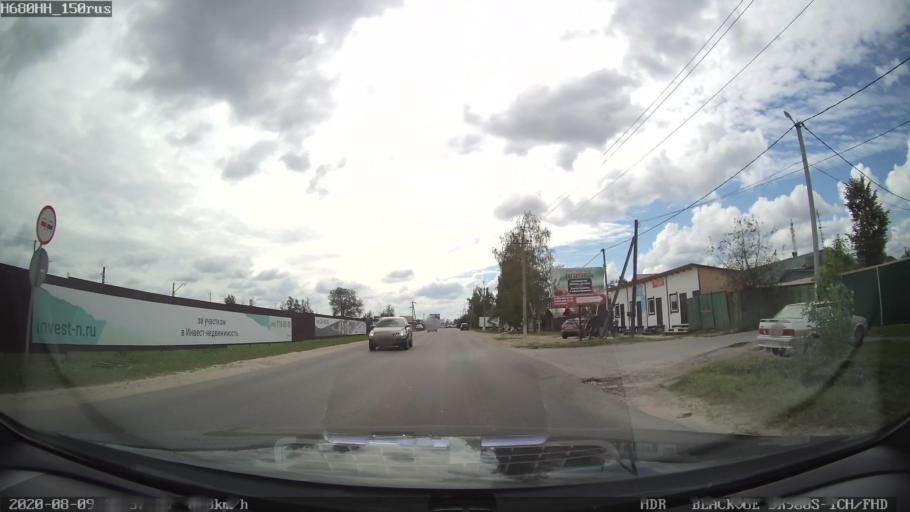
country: RU
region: Tula
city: Zaokskiy
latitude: 54.7389
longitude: 37.3953
